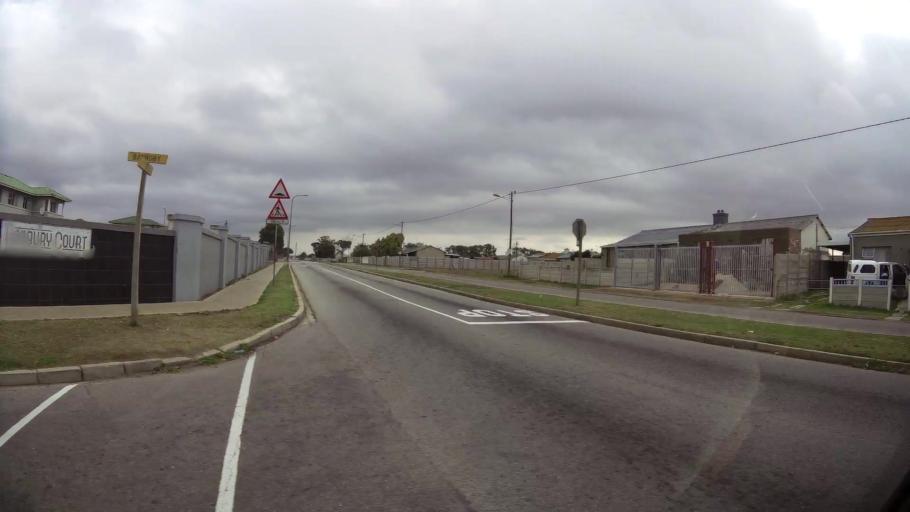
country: ZA
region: Eastern Cape
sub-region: Nelson Mandela Bay Metropolitan Municipality
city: Port Elizabeth
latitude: -33.9056
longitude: 25.5682
